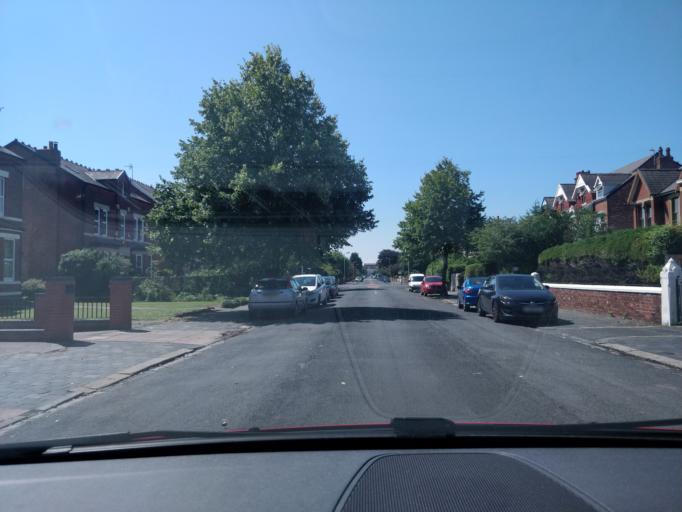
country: GB
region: England
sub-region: Sefton
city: Southport
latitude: 53.6574
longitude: -2.9950
